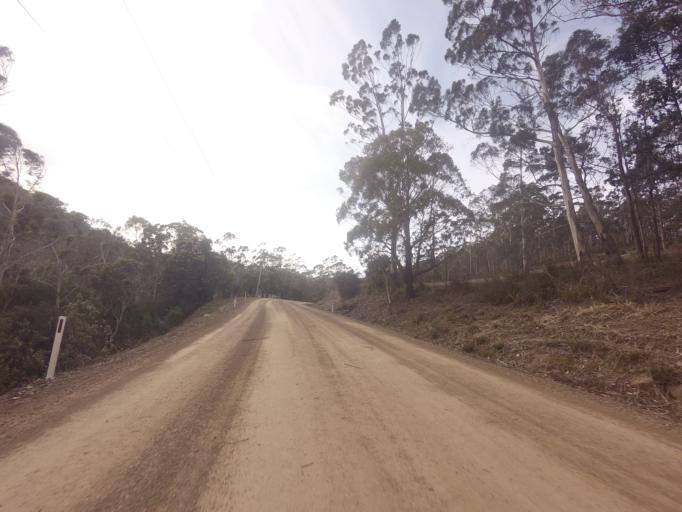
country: AU
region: Tasmania
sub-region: Huon Valley
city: Huonville
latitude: -43.0531
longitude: 147.1045
